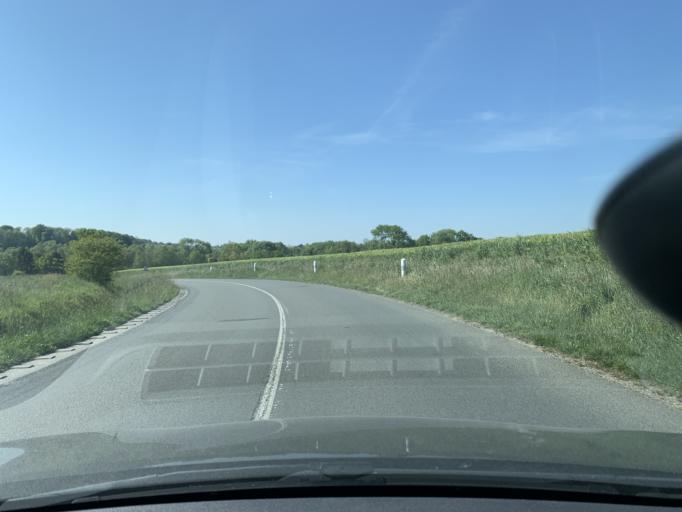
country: FR
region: Nord-Pas-de-Calais
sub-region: Departement du Nord
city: Masnieres
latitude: 50.0799
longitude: 3.2154
